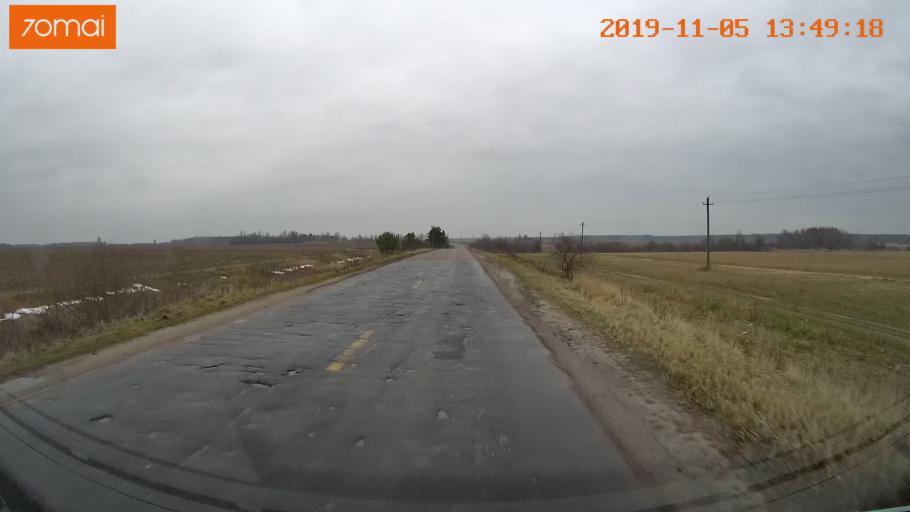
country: RU
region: Ivanovo
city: Kaminskiy
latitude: 57.0092
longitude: 41.4090
